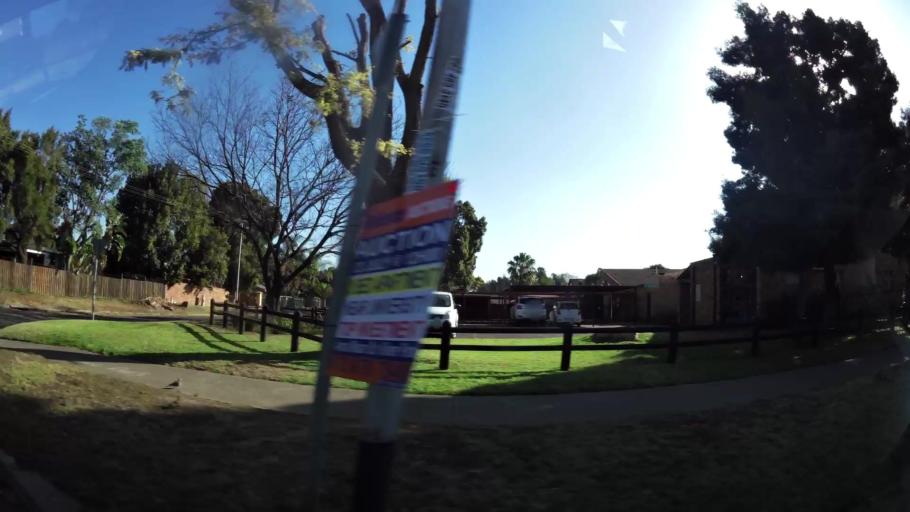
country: ZA
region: Gauteng
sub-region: City of Tshwane Metropolitan Municipality
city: Pretoria
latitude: -25.7209
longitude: 28.2611
